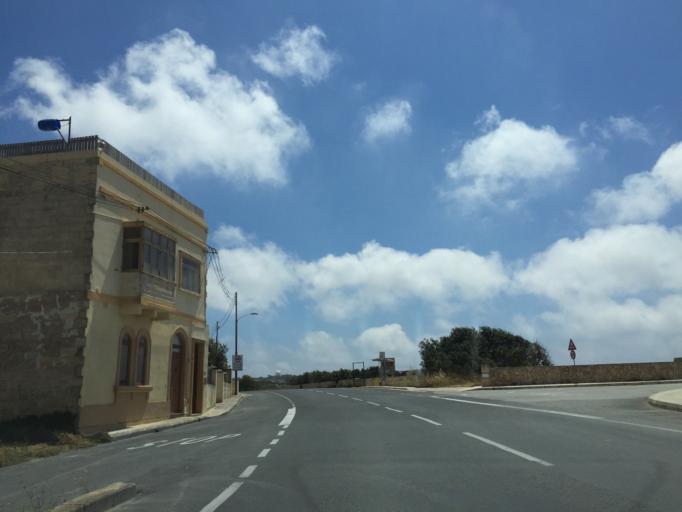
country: MT
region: Dingli
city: Dingli
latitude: 35.8704
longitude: 14.3913
